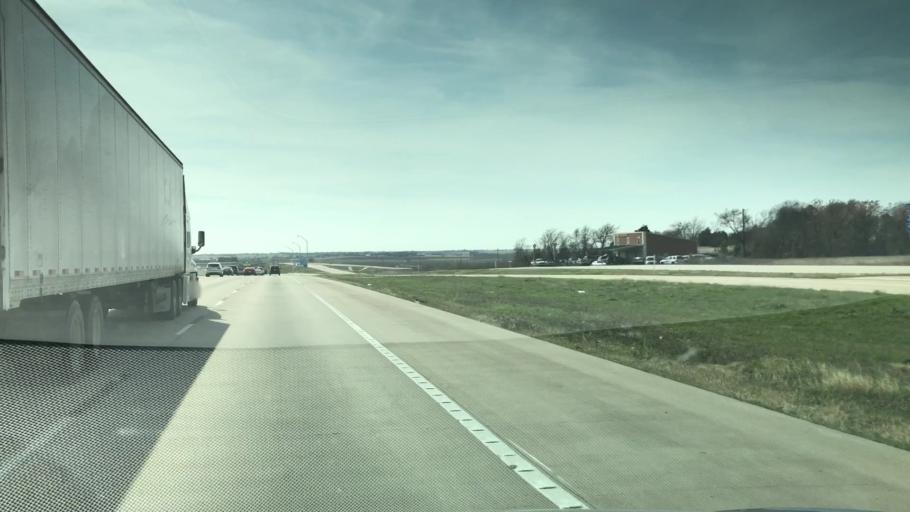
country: US
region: Texas
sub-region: McLennan County
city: West
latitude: 31.8272
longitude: -97.0959
